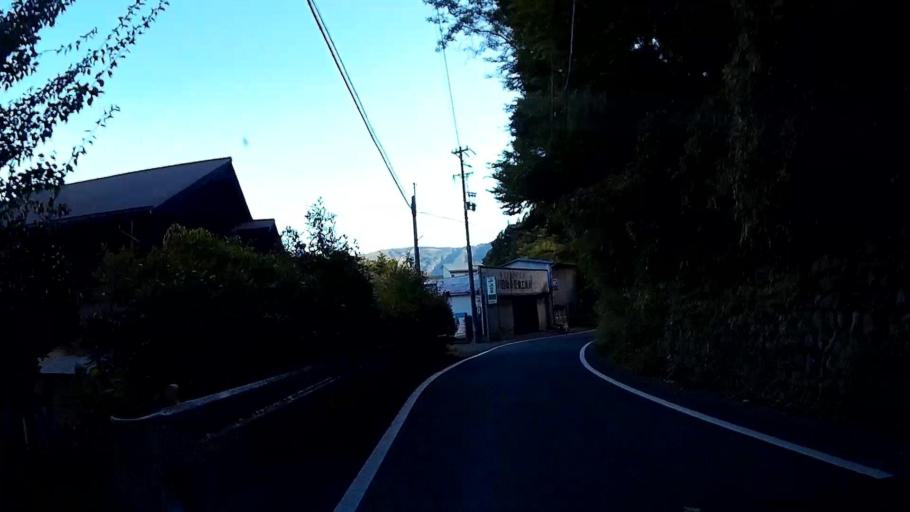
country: JP
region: Shizuoka
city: Shizuoka-shi
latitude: 35.2261
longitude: 138.2440
